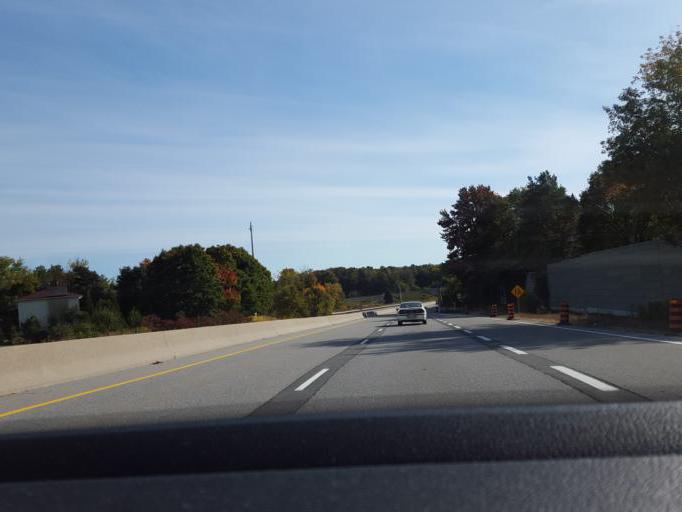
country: CA
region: Ontario
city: Oshawa
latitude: 43.9730
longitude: -78.6104
